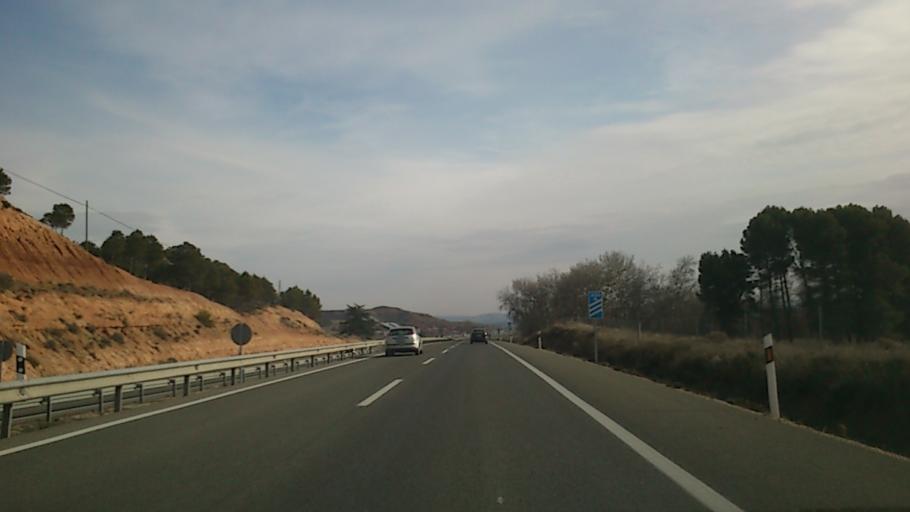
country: ES
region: Aragon
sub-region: Provincia de Zaragoza
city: Ariza
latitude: 41.3162
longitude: -2.0137
